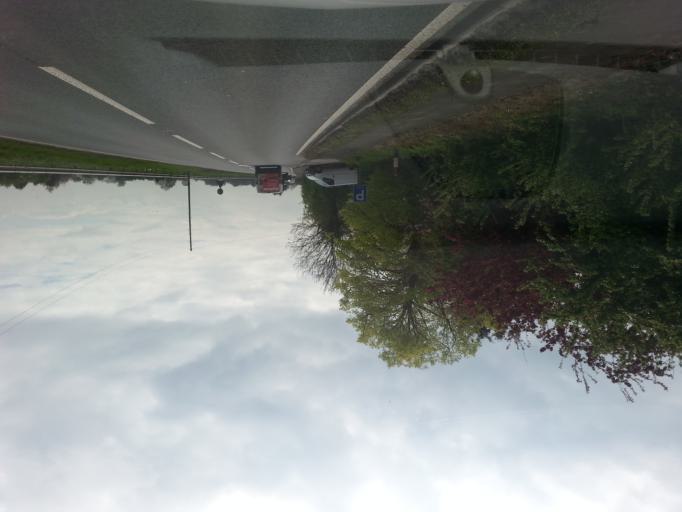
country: GB
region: England
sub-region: Cambridgeshire
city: Wisbech
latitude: 52.6414
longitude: 0.1300
